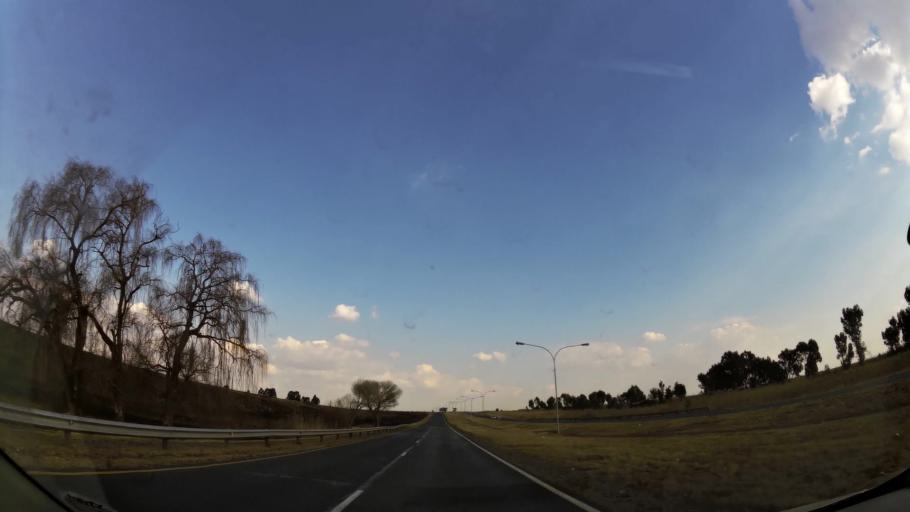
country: ZA
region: Gauteng
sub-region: Ekurhuleni Metropolitan Municipality
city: Springs
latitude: -26.3638
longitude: 28.3413
